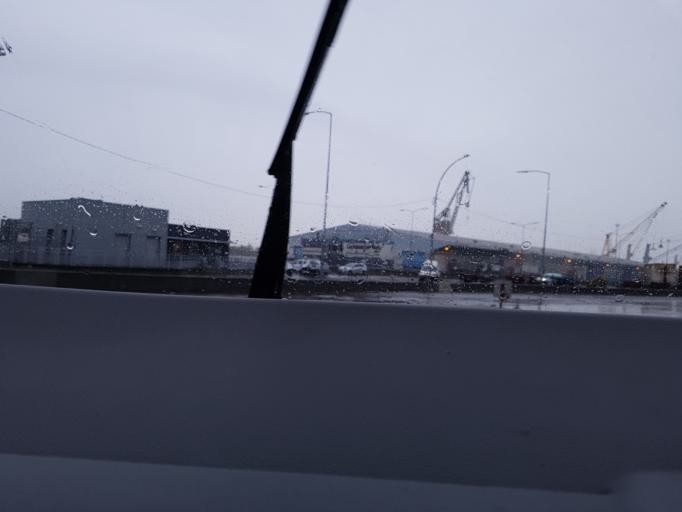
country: FR
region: Aquitaine
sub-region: Departement de la Gironde
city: Bassens
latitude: 44.9042
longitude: -0.5348
